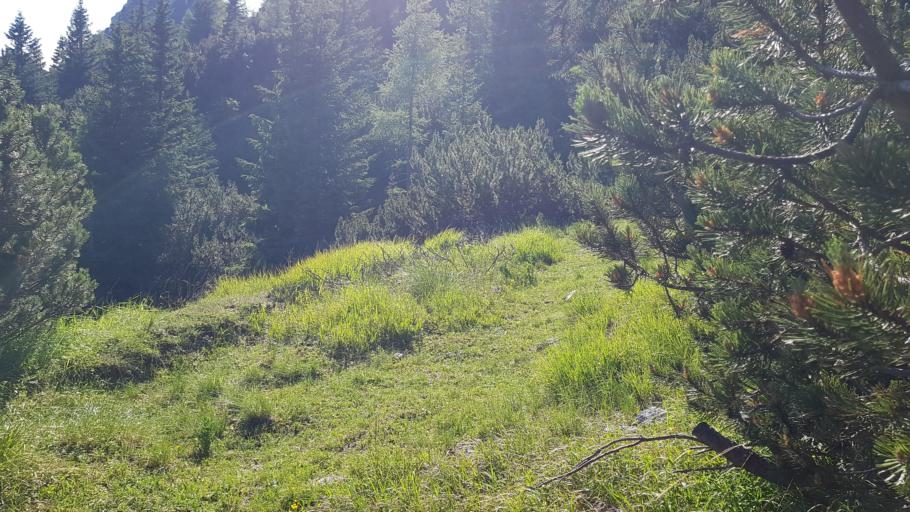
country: IT
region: Friuli Venezia Giulia
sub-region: Provincia di Udine
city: Malborghetto
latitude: 46.4768
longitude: 13.3925
